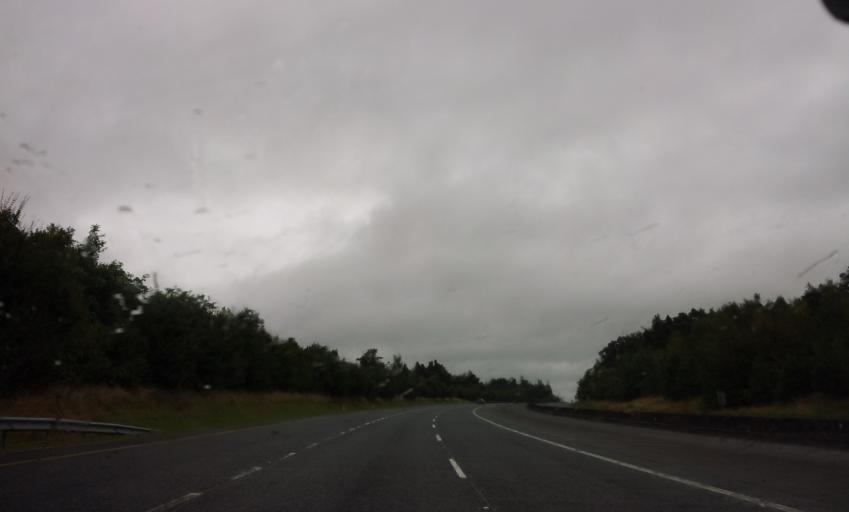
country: IE
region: Munster
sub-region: County Cork
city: Fermoy
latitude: 52.1186
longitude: -8.2713
